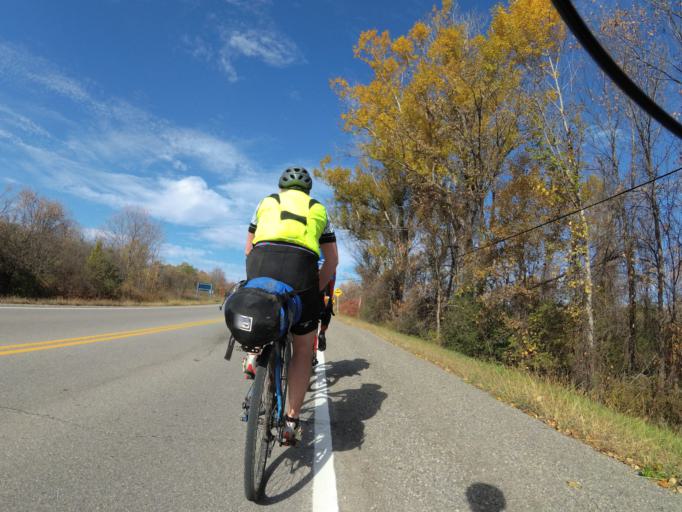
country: CA
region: Ontario
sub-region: Lanark County
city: Smiths Falls
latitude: 44.8955
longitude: -76.0159
